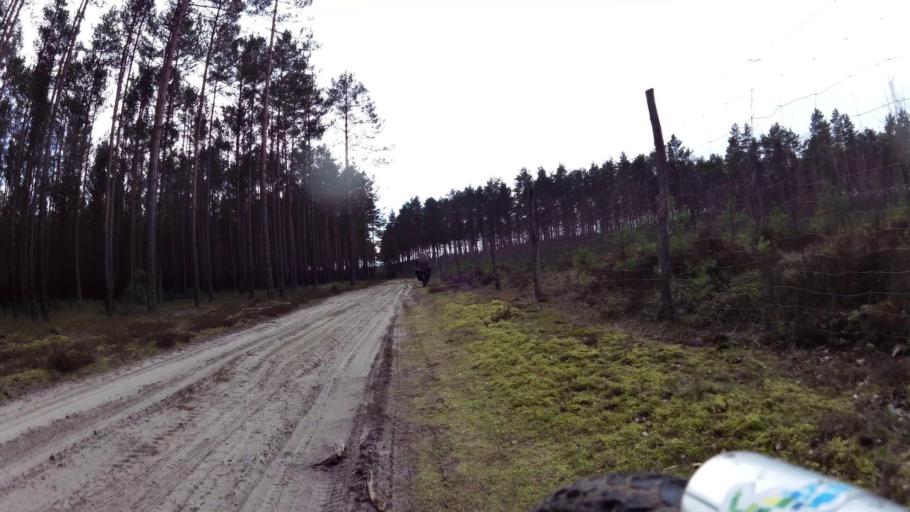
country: PL
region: Pomeranian Voivodeship
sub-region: Powiat bytowski
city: Kolczyglowy
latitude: 54.1664
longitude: 17.1950
